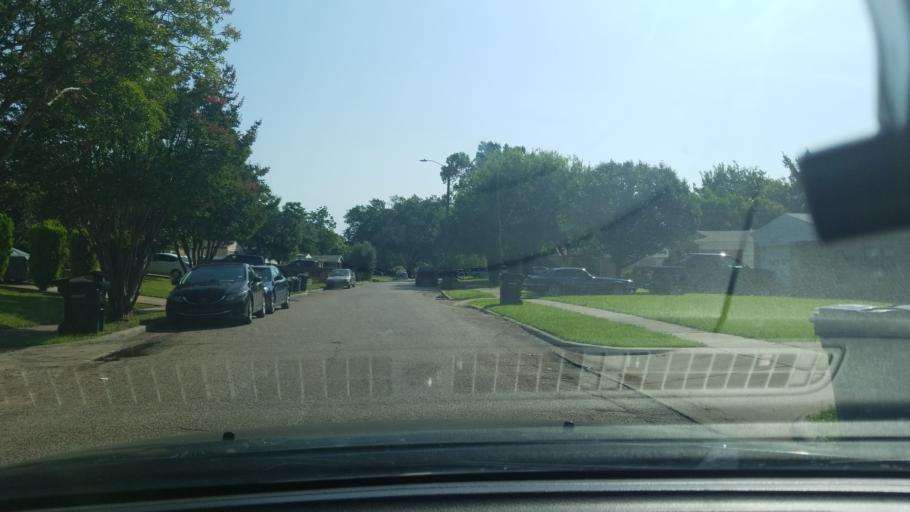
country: US
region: Texas
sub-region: Dallas County
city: Mesquite
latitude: 32.8299
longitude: -96.6450
